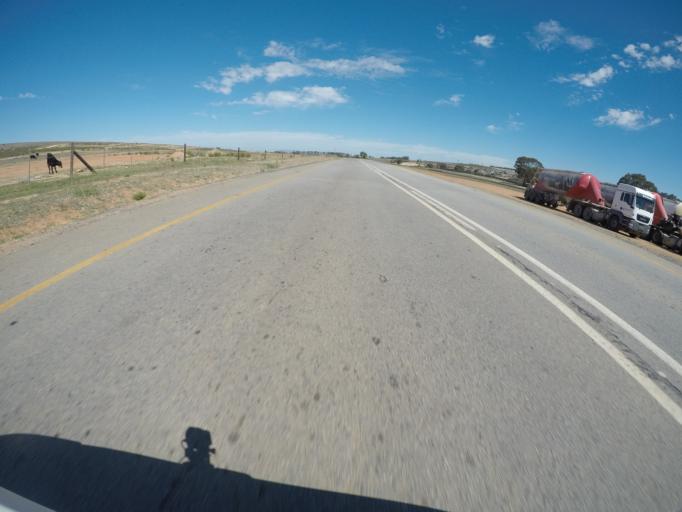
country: ZA
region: Western Cape
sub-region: West Coast District Municipality
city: Malmesbury
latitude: -33.4918
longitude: 18.6834
